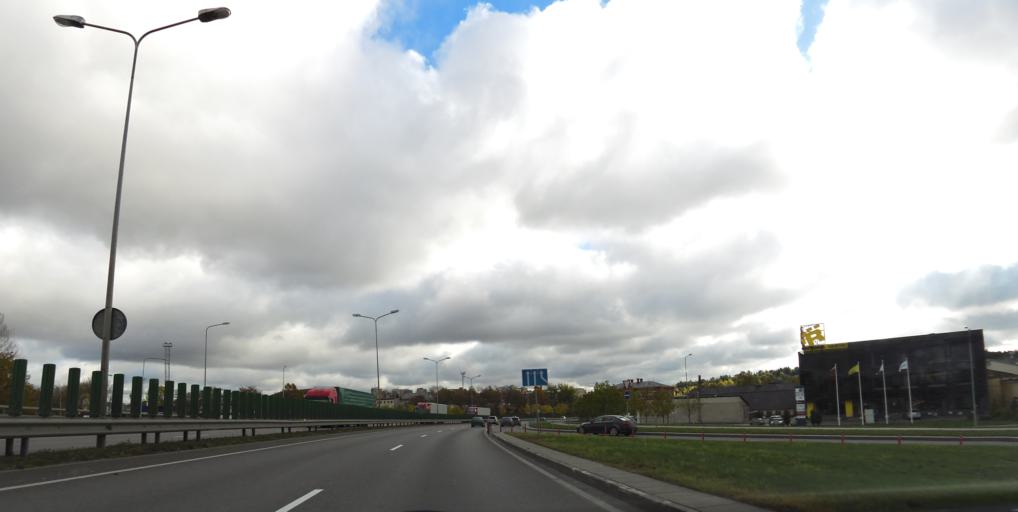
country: LT
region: Vilnius County
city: Vilkpede
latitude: 54.6661
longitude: 25.2517
